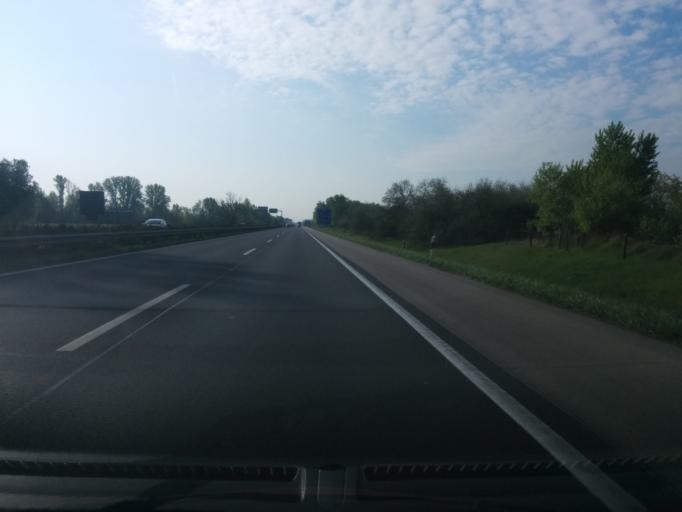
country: HU
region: Pest
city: Gyal
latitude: 47.3894
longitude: 19.1727
